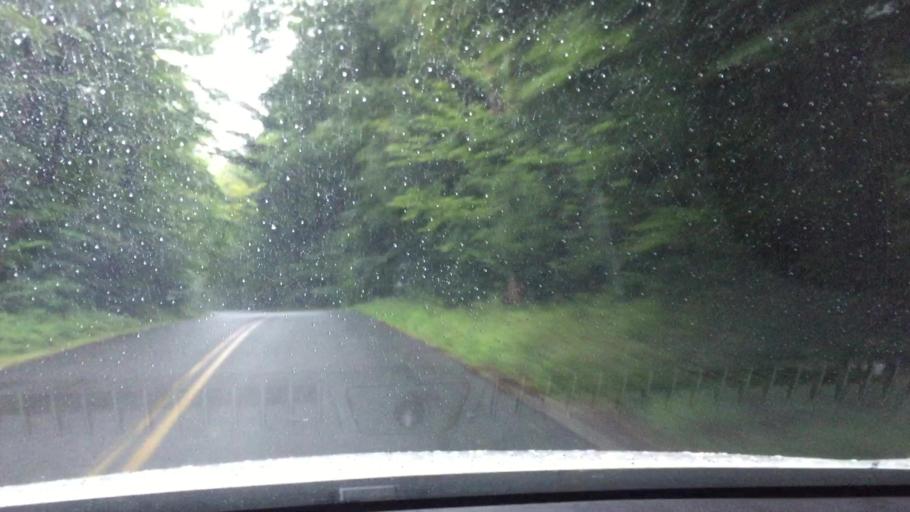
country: US
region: Massachusetts
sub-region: Berkshire County
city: Becket
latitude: 42.2755
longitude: -73.0251
